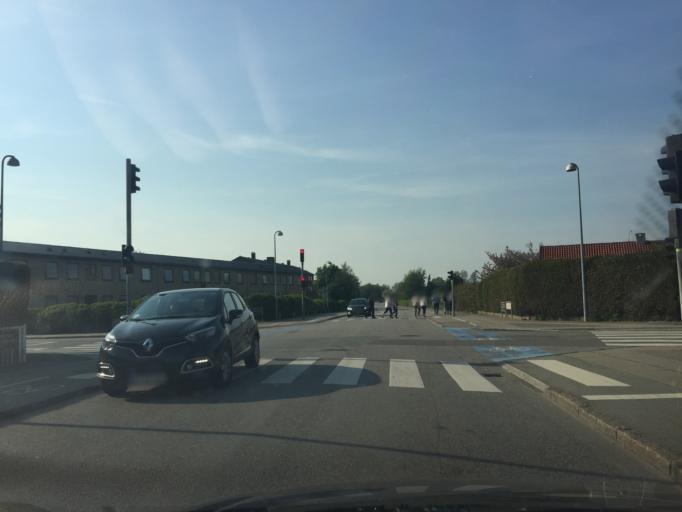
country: DK
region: Capital Region
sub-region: Hoje-Taastrup Kommune
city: Flong
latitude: 55.6533
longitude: 12.1997
